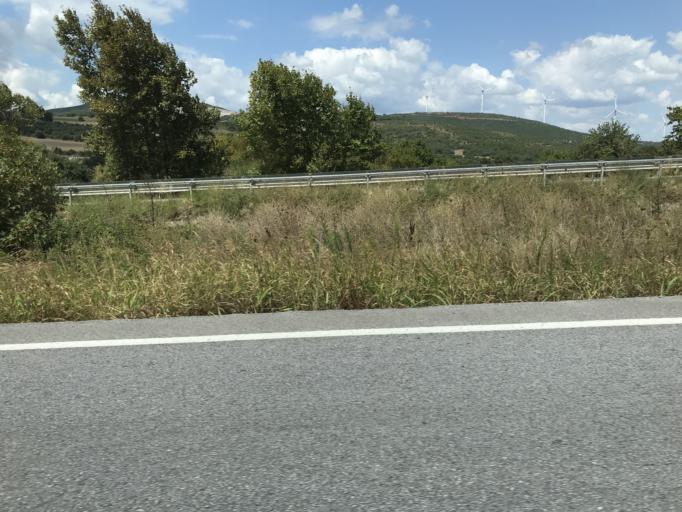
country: TR
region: Balikesir
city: Yenikoy
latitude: 39.7794
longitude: 28.0451
